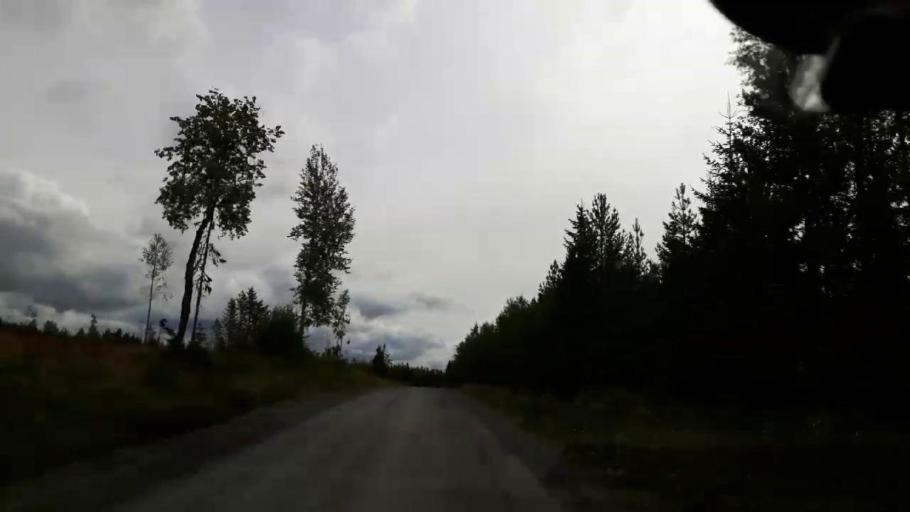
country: SE
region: Jaemtland
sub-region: Krokoms Kommun
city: Valla
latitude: 63.6529
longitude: 13.9819
